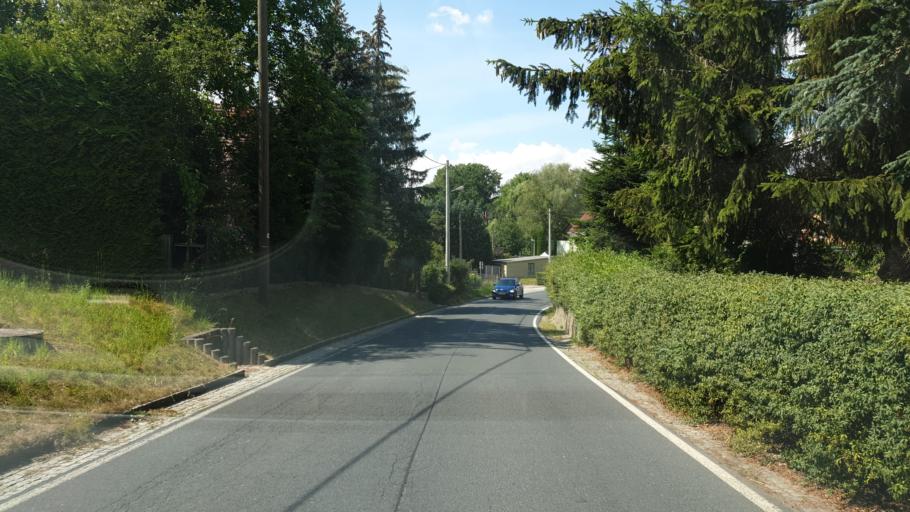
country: DE
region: Saxony
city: Radeberg
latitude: 51.0406
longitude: 13.9254
